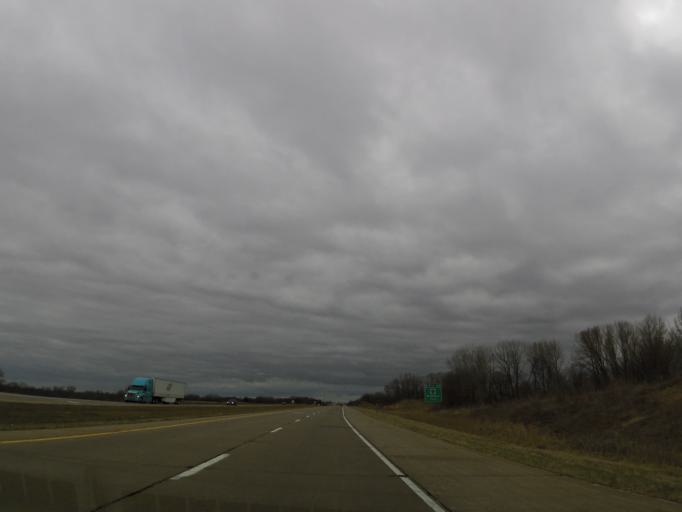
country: US
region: Iowa
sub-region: Benton County
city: Urbana
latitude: 42.3273
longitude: -91.9965
